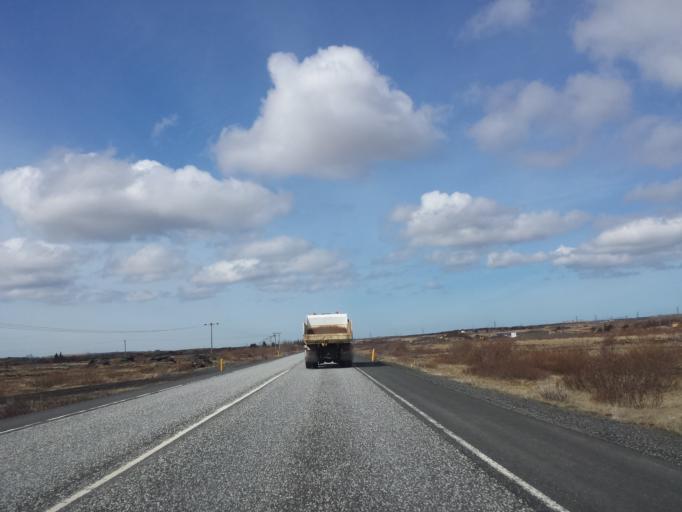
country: IS
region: Capital Region
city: Mosfellsbaer
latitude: 64.0796
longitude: -21.6634
